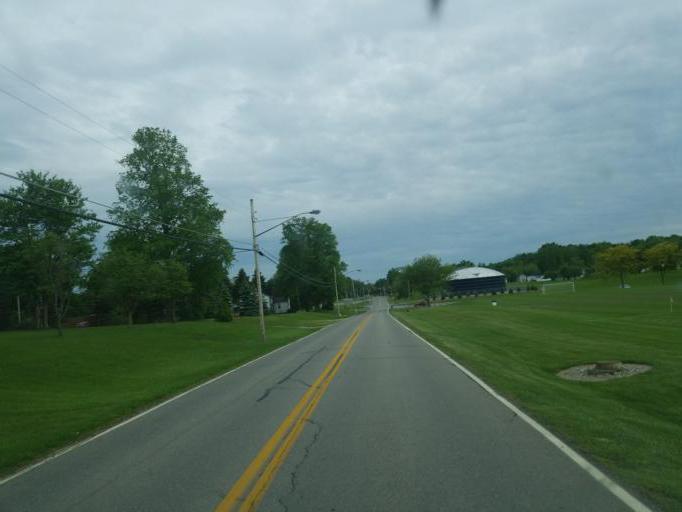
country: US
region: Ohio
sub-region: Richland County
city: Ontario
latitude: 40.7635
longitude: -82.6326
